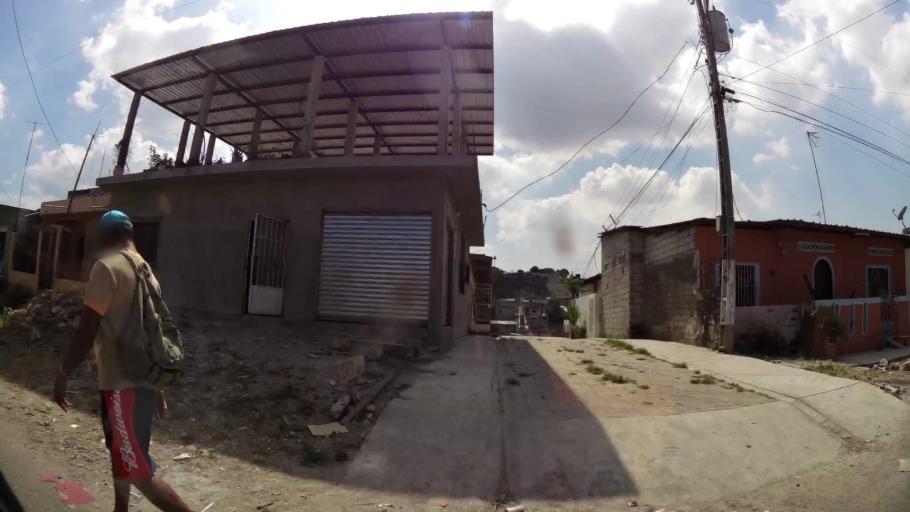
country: EC
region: Guayas
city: Santa Lucia
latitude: -2.1348
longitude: -79.9440
